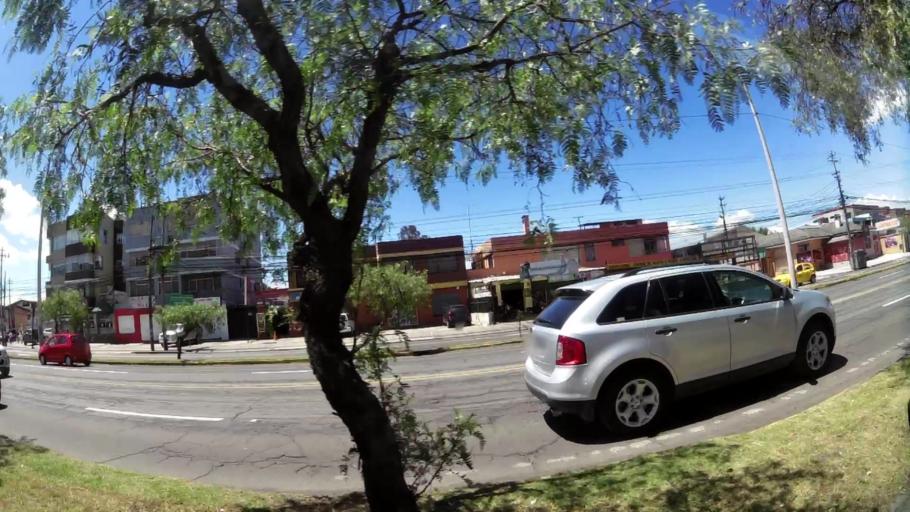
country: EC
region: Pichincha
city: Quito
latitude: -0.1509
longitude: -78.4843
